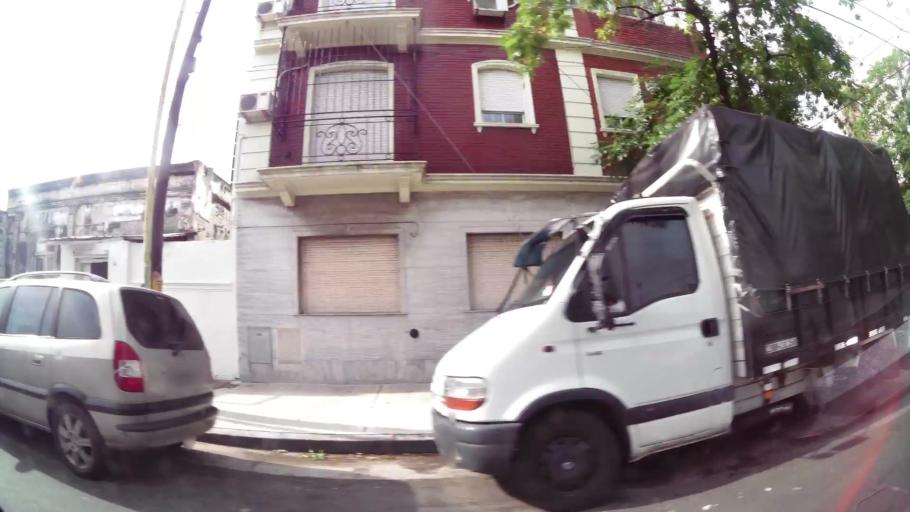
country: AR
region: Buenos Aires F.D.
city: Buenos Aires
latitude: -34.6442
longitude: -58.4175
